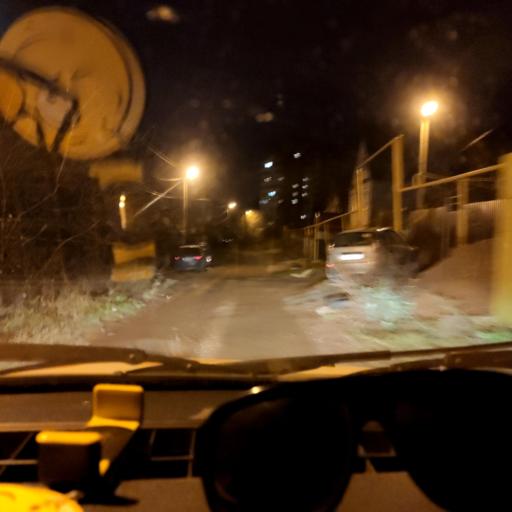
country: RU
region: Bashkortostan
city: Ufa
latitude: 54.7794
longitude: 56.0450
